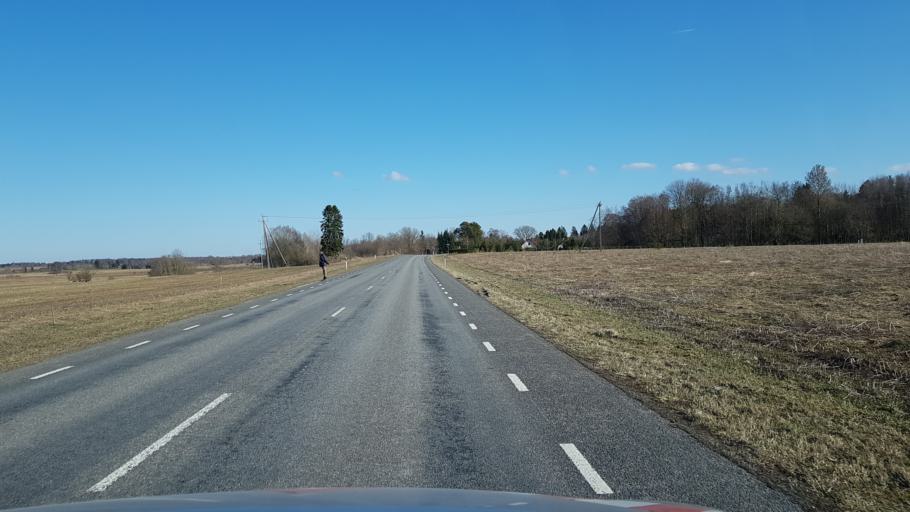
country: EE
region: Laeaene-Virumaa
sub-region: Haljala vald
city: Haljala
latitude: 59.4493
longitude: 26.2452
